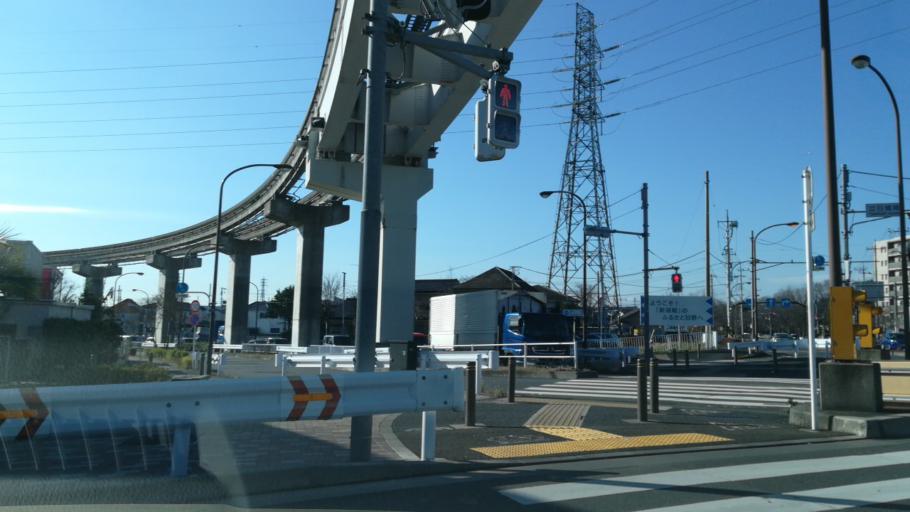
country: JP
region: Tokyo
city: Hino
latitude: 35.6815
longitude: 139.4059
